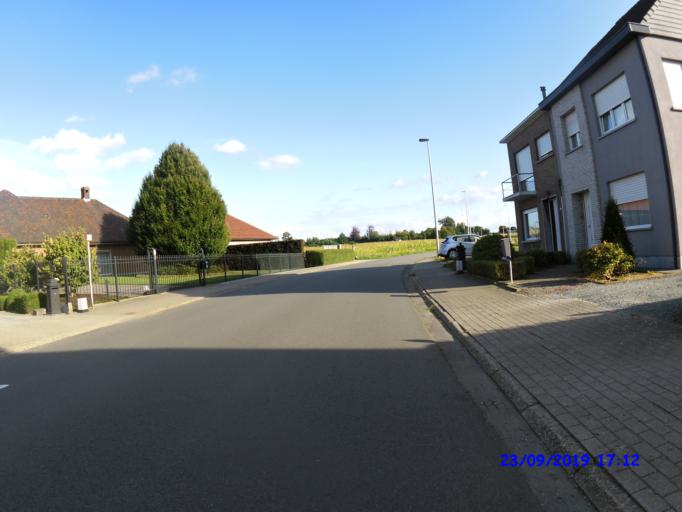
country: BE
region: Flanders
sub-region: Provincie Oost-Vlaanderen
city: Haaltert
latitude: 50.9301
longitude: 3.9802
